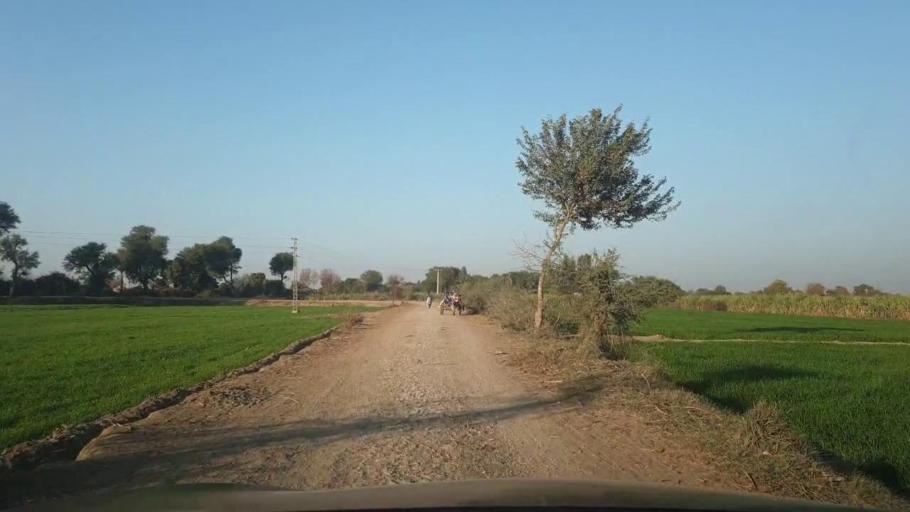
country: PK
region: Sindh
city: Mirpur Mathelo
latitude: 28.1529
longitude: 69.5646
